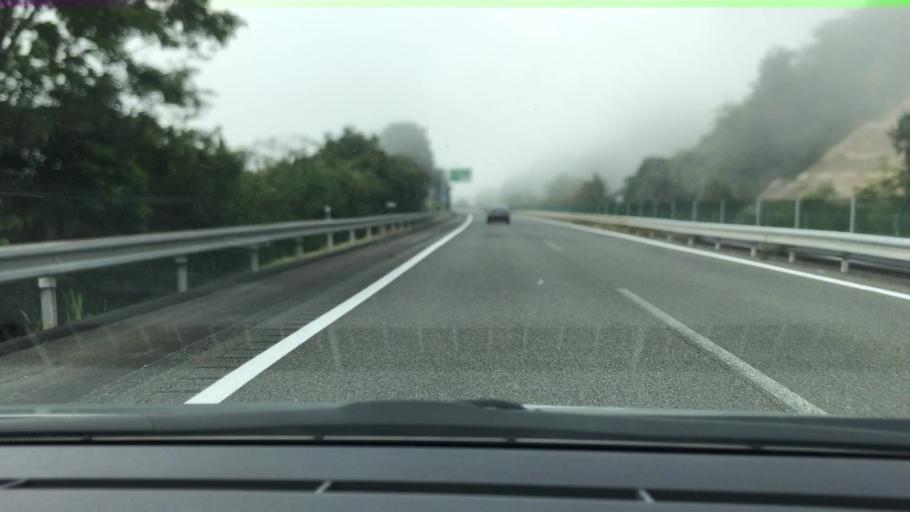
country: JP
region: Hyogo
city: Sasayama
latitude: 35.0975
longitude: 135.1692
